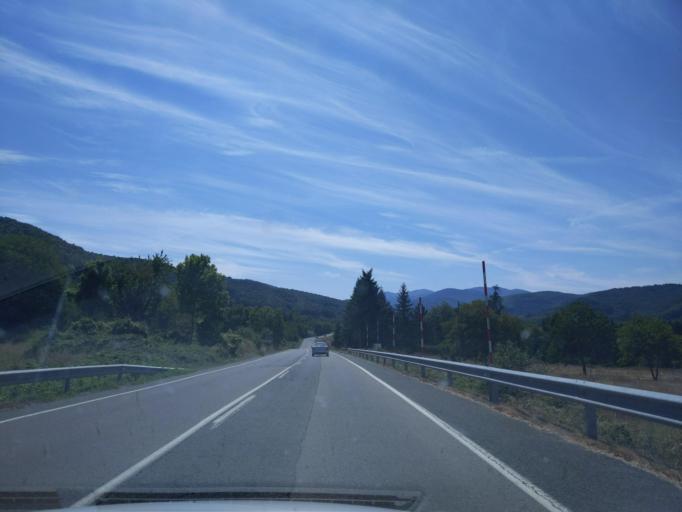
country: ES
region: La Rioja
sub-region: Provincia de La Rioja
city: Santurdejo
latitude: 42.3711
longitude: -2.9803
